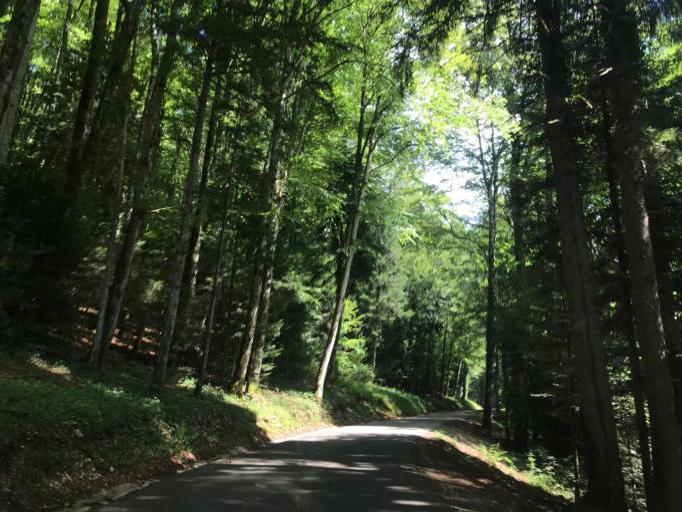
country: FR
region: Franche-Comte
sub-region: Departement du Jura
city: Moirans-en-Montagne
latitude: 46.4980
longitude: 5.7659
